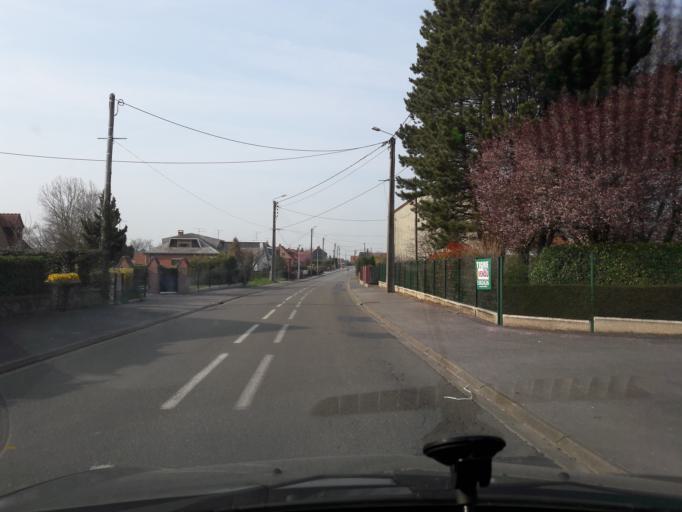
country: FR
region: Nord-Pas-de-Calais
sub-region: Departement du Nord
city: Rousies
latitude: 50.2618
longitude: 4.0086
